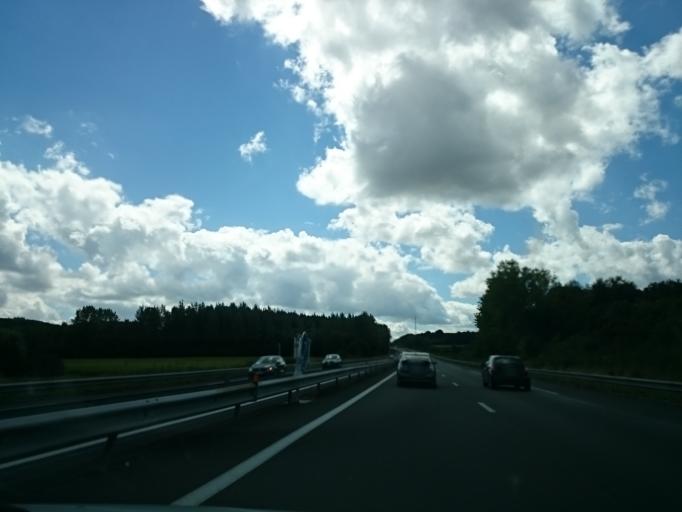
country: FR
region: Pays de la Loire
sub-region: Departement de Maine-et-Loire
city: Seiches-sur-le-Loir
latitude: 47.6150
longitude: -0.2922
